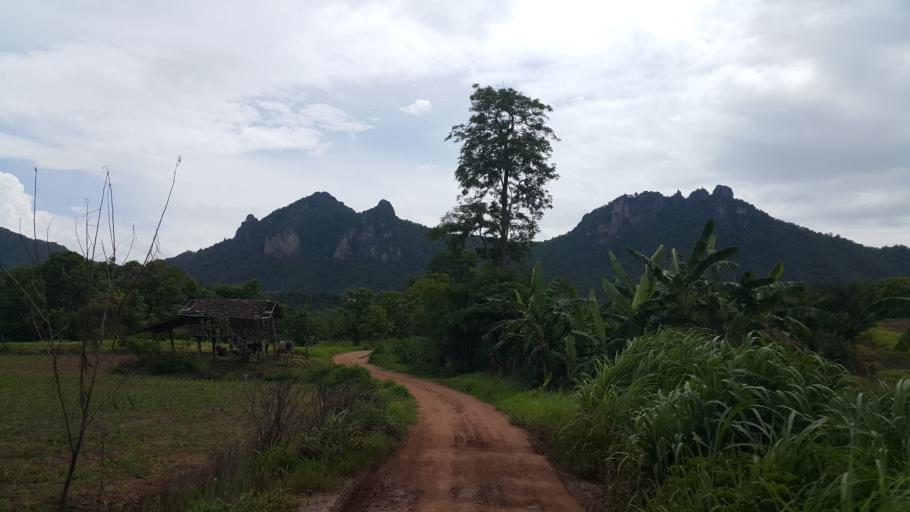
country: TH
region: Lampang
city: Chae Hom
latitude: 18.7465
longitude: 99.5524
